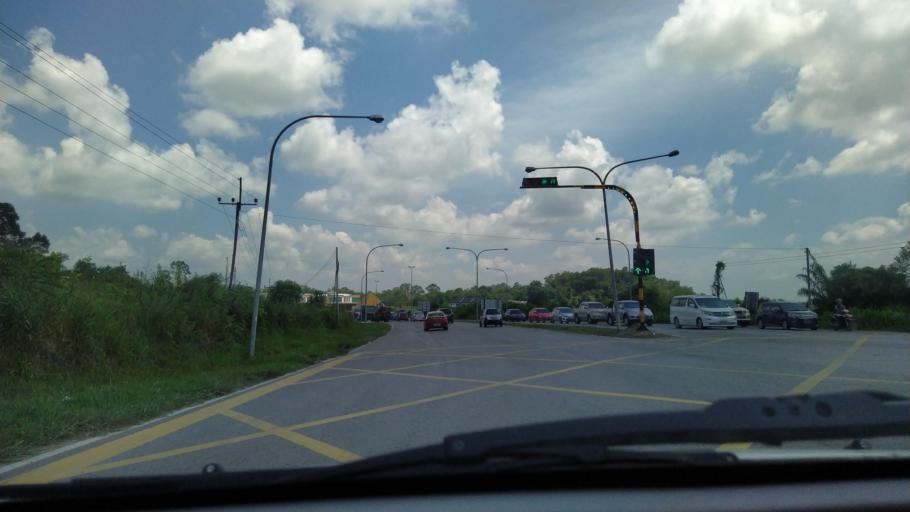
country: MY
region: Sarawak
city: Sibu
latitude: 2.2922
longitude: 111.9422
